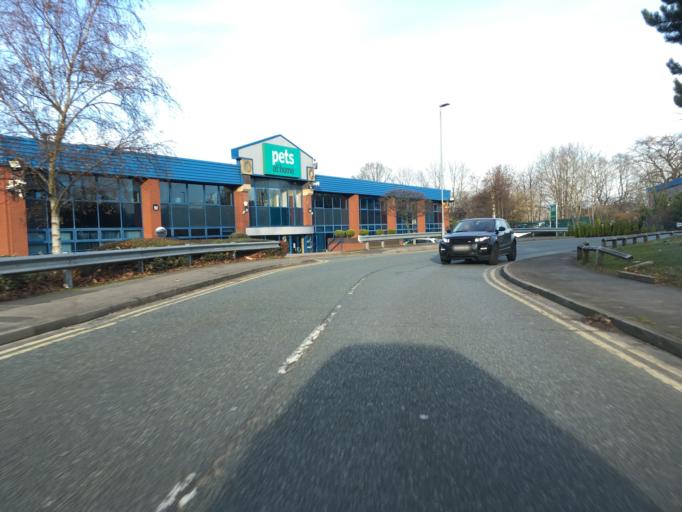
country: GB
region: England
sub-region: Borough of Stockport
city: Cheadle Hulme
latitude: 53.3517
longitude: -2.2089
